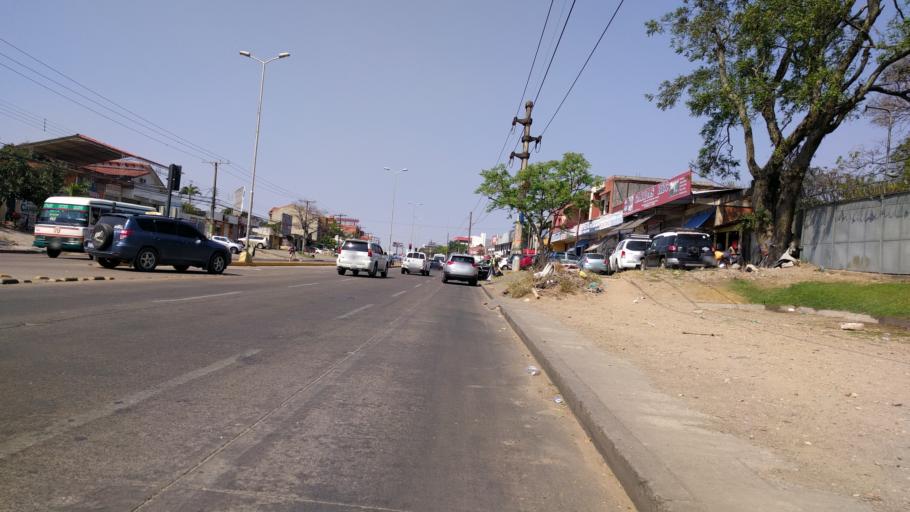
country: BO
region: Santa Cruz
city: Santa Cruz de la Sierra
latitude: -17.7994
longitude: -63.2023
